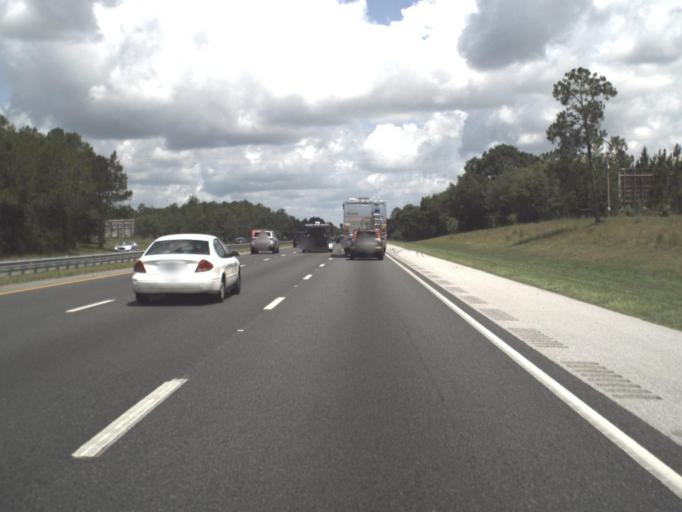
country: US
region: Florida
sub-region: Suwannee County
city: Wellborn
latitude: 30.3292
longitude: -82.8190
